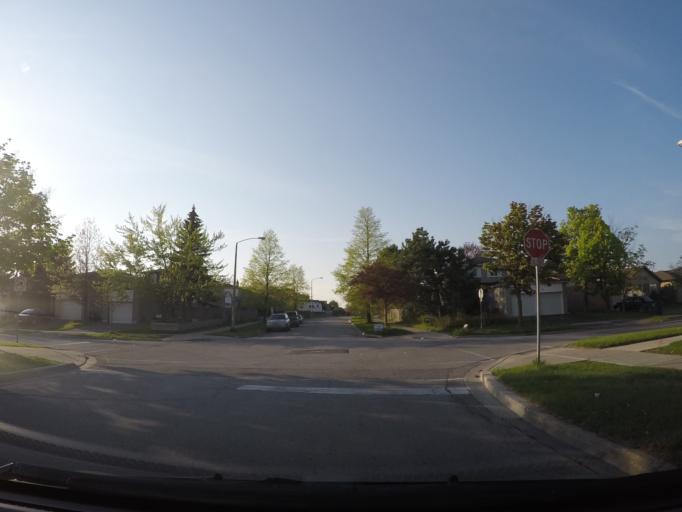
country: CA
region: Ontario
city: Markham
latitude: 43.8215
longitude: -79.2660
